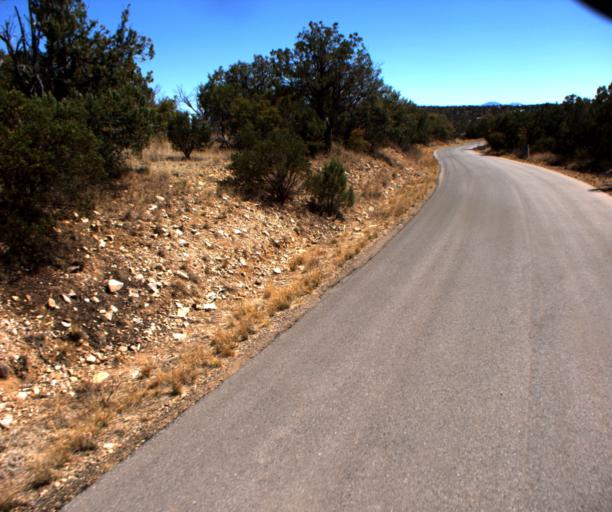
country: US
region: Arizona
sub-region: Cochise County
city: Sierra Vista
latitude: 31.4399
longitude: -110.4408
